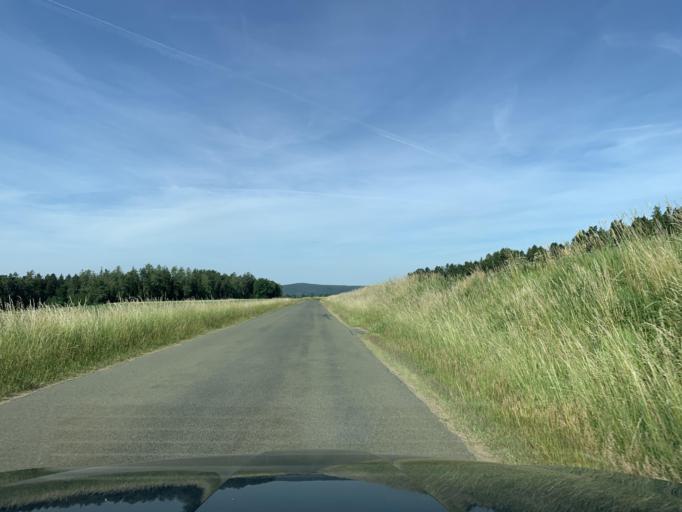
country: DE
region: Bavaria
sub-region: Upper Palatinate
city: Bach
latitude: 49.4075
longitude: 12.3572
